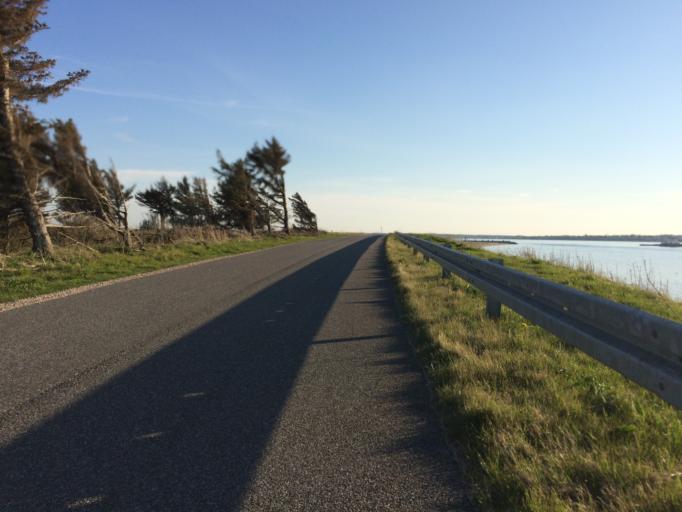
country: DK
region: Central Jutland
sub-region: Struer Kommune
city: Struer
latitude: 56.5200
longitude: 8.6261
